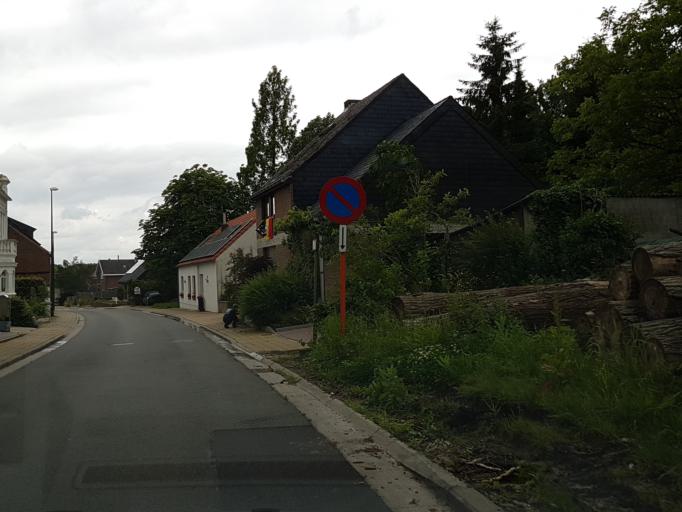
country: BE
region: Flanders
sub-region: Provincie Oost-Vlaanderen
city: Denderleeuw
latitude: 50.9019
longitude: 4.0799
